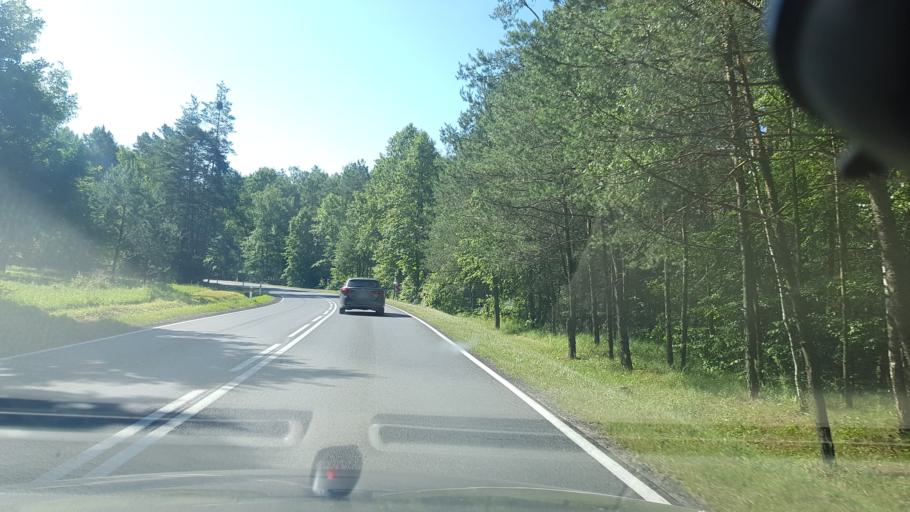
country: PL
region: Masovian Voivodeship
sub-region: Powiat wyszkowski
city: Branszczyk
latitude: 52.5701
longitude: 21.5433
